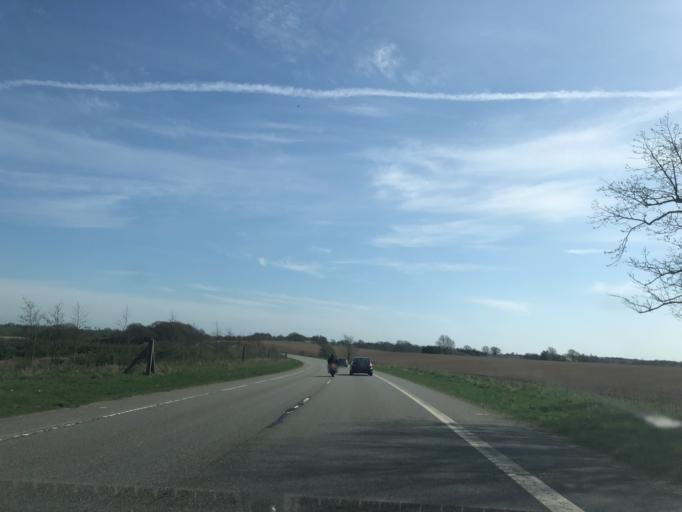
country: DK
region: Zealand
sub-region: Faxe Kommune
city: Haslev
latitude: 55.3081
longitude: 11.9842
